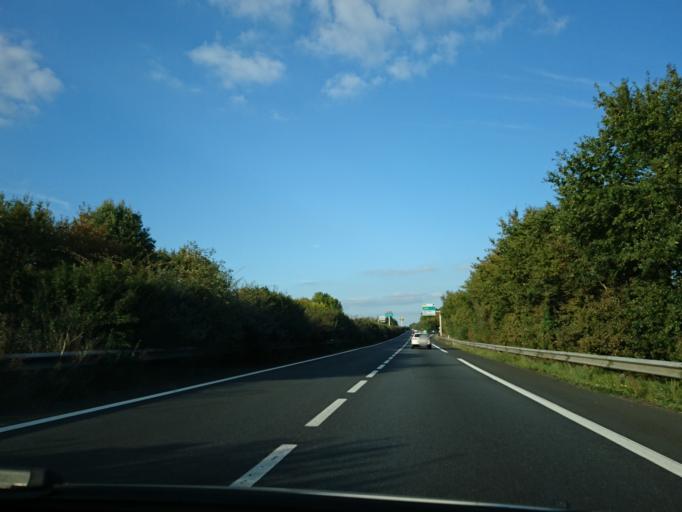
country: FR
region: Pays de la Loire
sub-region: Departement de la Loire-Atlantique
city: Nozay
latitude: 47.5748
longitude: -1.6314
